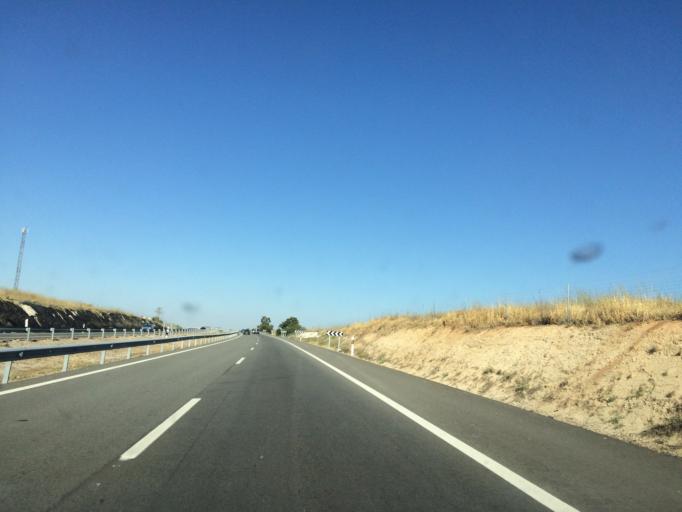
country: ES
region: Castille-La Mancha
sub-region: Province of Toledo
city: Torralba de Oropesa
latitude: 39.9316
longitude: -5.1468
